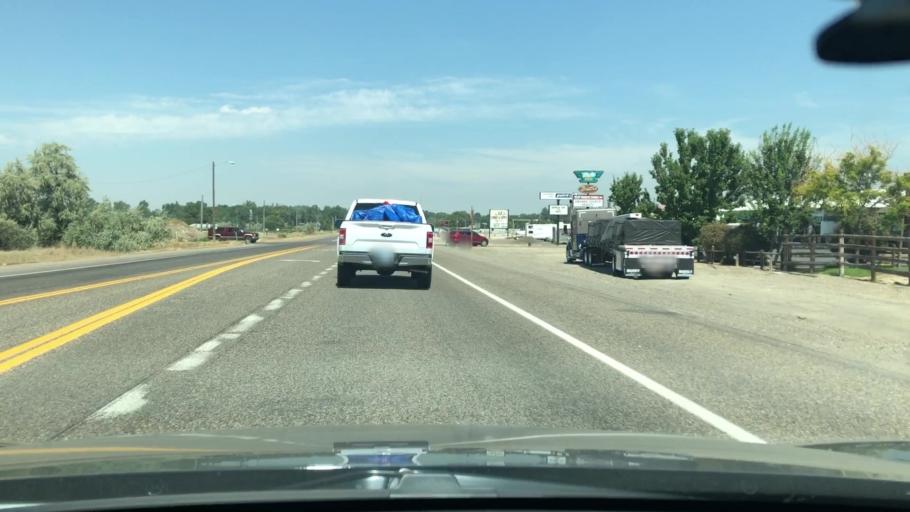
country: US
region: Idaho
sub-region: Owyhee County
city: Homedale
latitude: 43.6133
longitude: -116.9282
